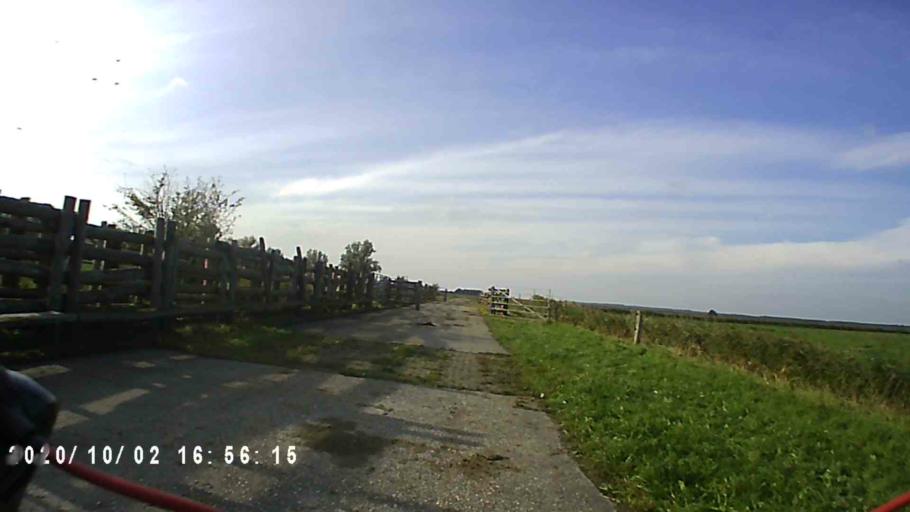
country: NL
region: Groningen
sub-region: Gemeente De Marne
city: Ulrum
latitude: 53.3420
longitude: 6.2631
